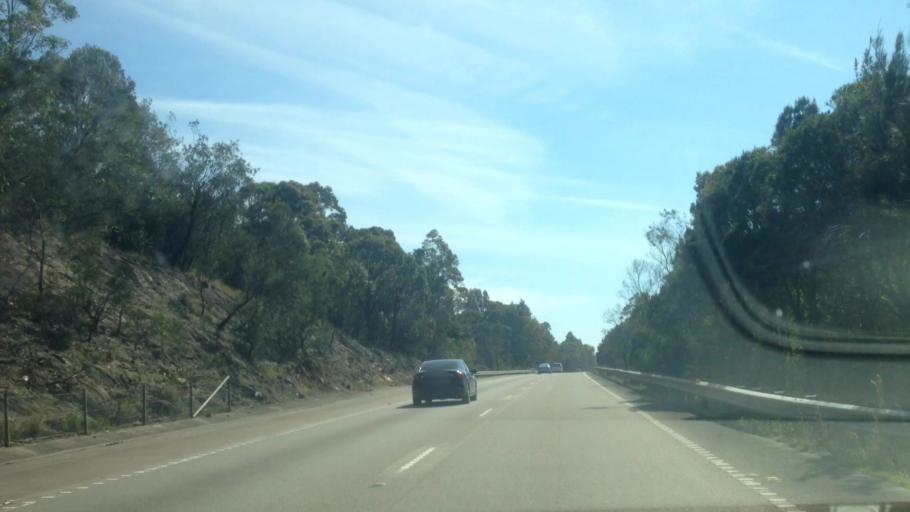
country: AU
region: New South Wales
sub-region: Lake Macquarie Shire
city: Fennell Bay
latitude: -32.9616
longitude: 151.5394
